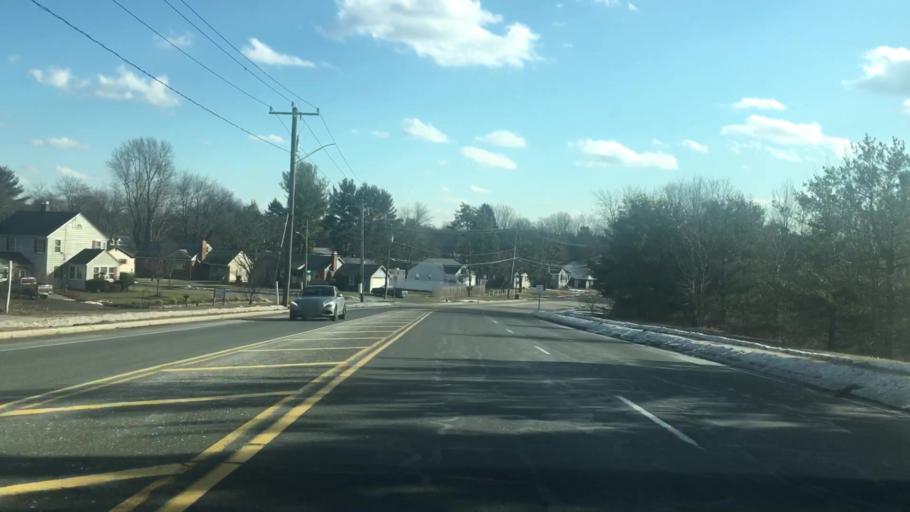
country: US
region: Connecticut
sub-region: Hartford County
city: East Hartford
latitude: 41.7707
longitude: -72.6016
